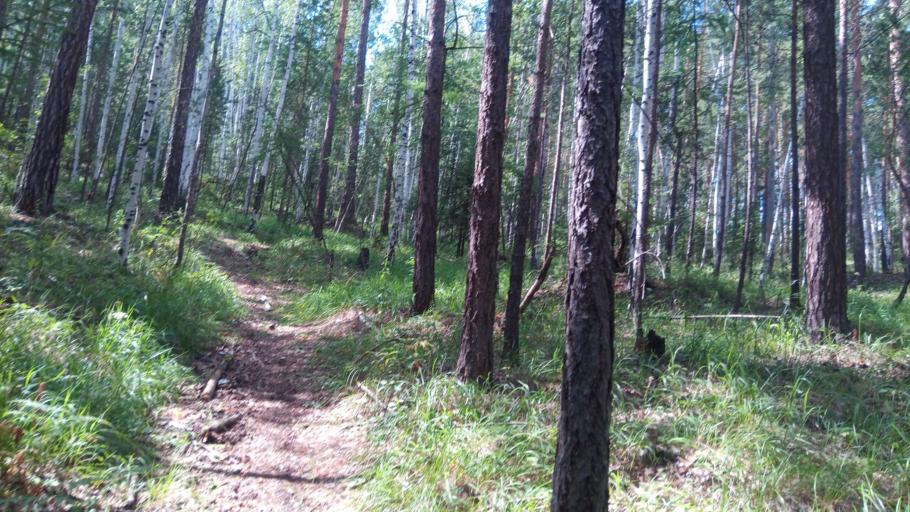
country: RU
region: Chelyabinsk
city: Karabash
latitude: 55.4027
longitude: 60.1361
